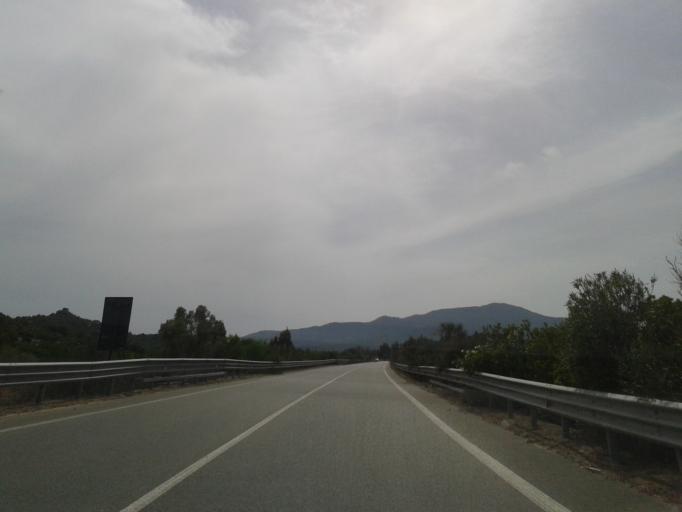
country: IT
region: Sardinia
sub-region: Provincia di Cagliari
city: Olia Speciosa
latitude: 39.2586
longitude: 9.5330
